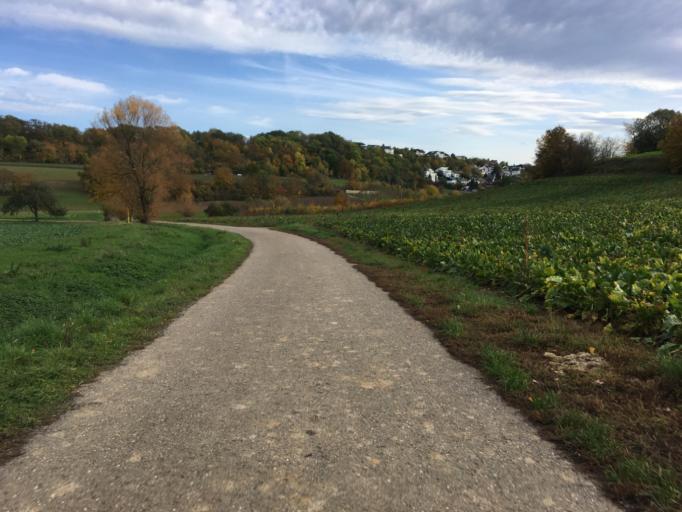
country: DE
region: Baden-Wuerttemberg
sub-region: Karlsruhe Region
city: Sinsheim
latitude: 49.2624
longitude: 8.9015
